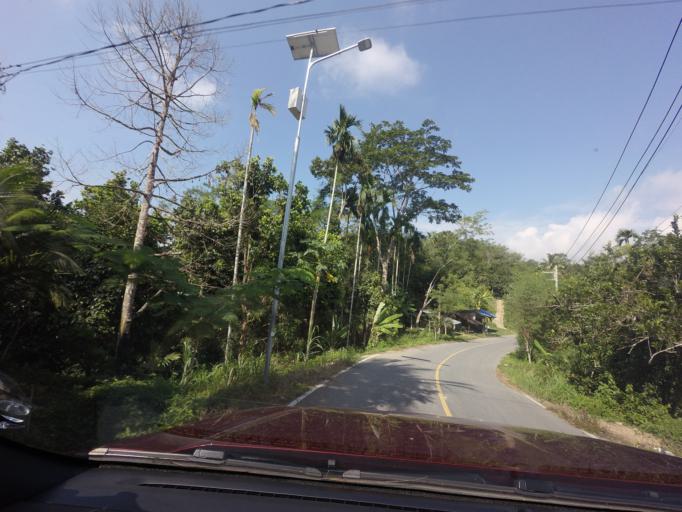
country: TH
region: Yala
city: Than To
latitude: 5.9980
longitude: 101.2182
